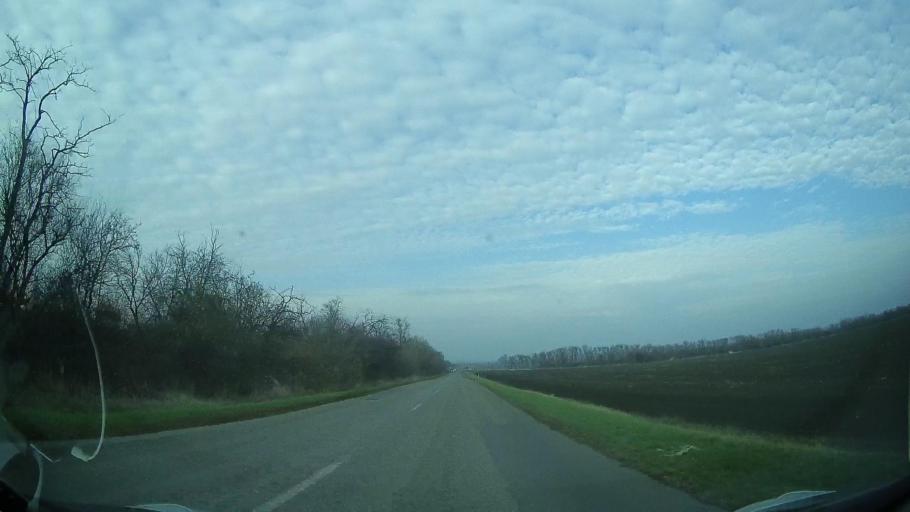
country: RU
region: Rostov
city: Bagayevskaya
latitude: 47.0885
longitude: 40.3915
